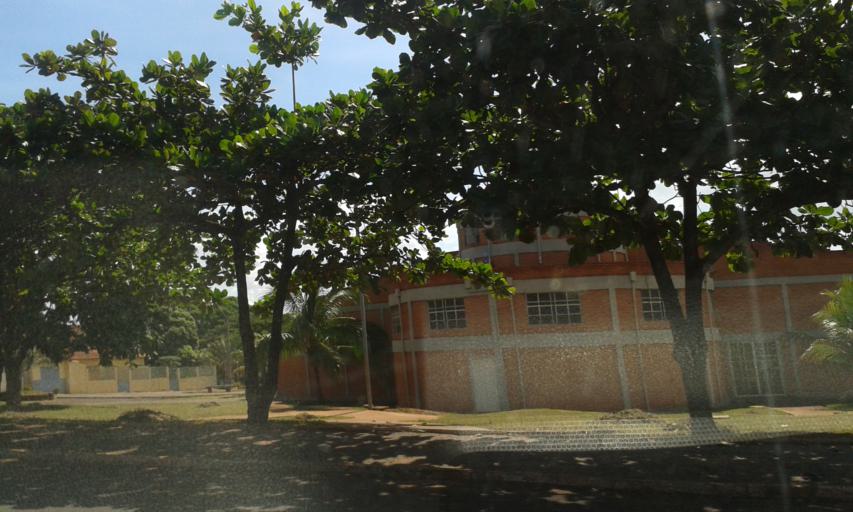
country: BR
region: Minas Gerais
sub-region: Santa Vitoria
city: Santa Vitoria
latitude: -18.8391
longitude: -50.1223
